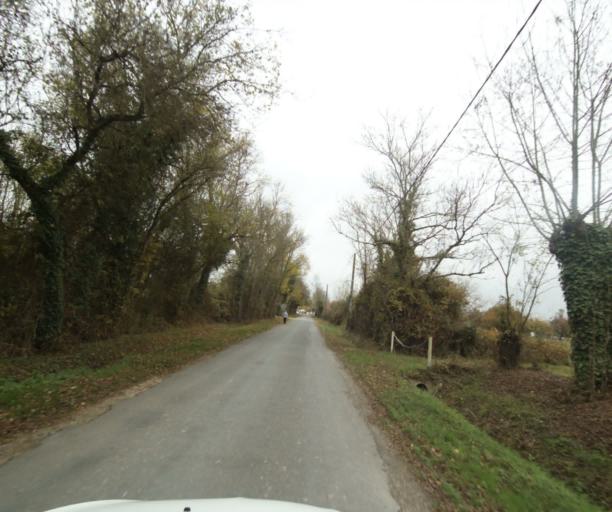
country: FR
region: Poitou-Charentes
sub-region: Departement de la Charente-Maritime
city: Saintes
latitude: 45.7353
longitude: -0.6266
